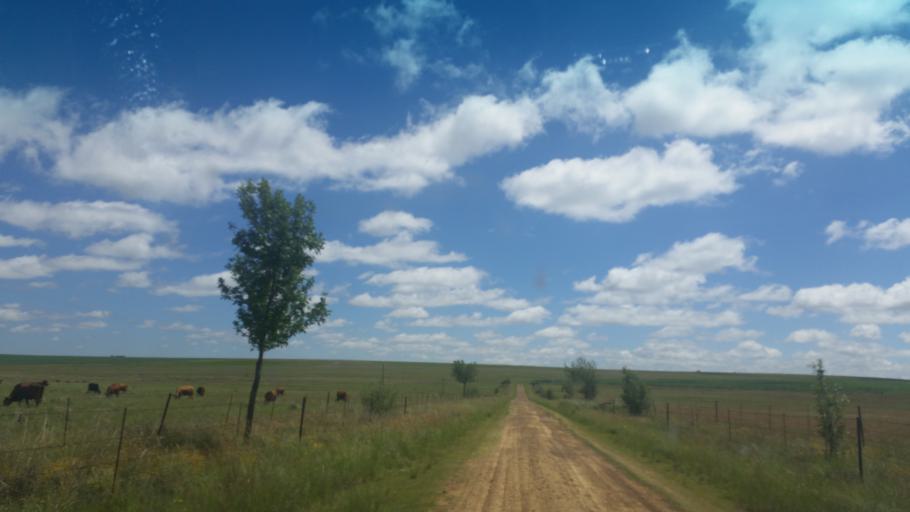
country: ZA
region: Orange Free State
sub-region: Thabo Mofutsanyana District Municipality
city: Harrismith
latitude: -28.1843
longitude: 29.0214
